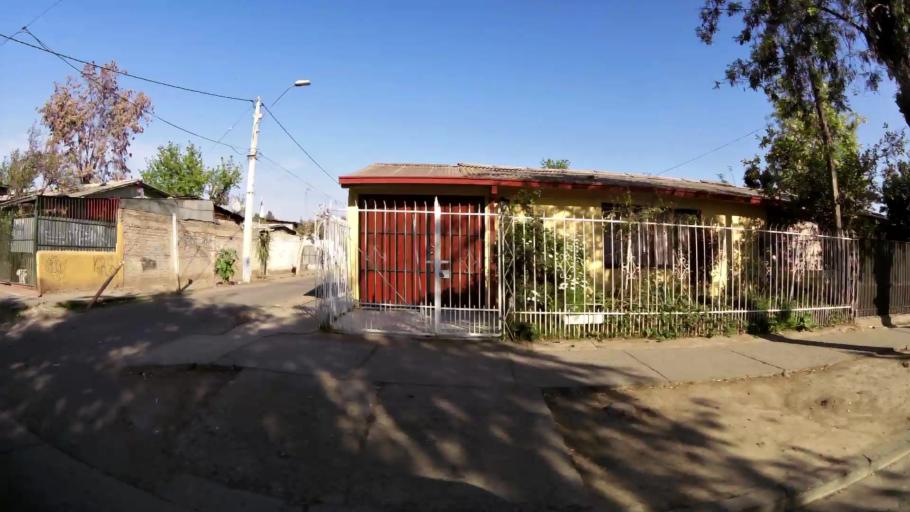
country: CL
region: Santiago Metropolitan
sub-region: Provincia de Santiago
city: Santiago
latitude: -33.3833
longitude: -70.6497
